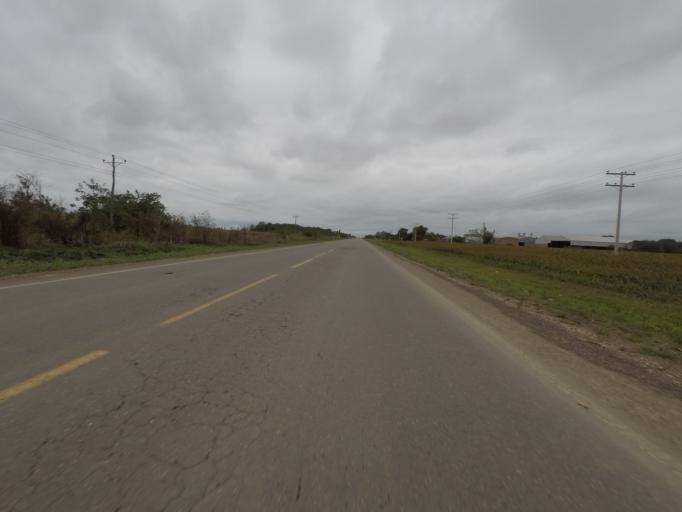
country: BO
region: Santa Cruz
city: Okinawa Numero Uno
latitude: -17.2444
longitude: -62.5554
